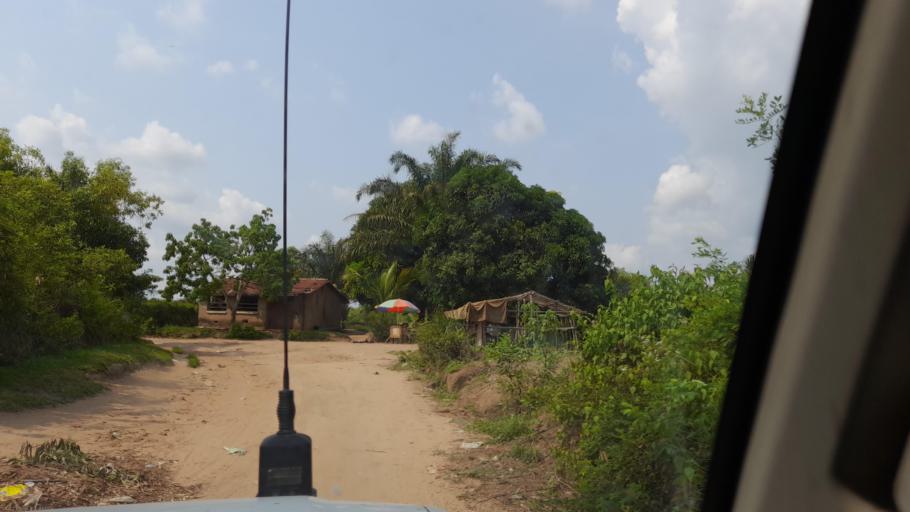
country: CD
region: Kasai-Occidental
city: Kananga
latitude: -5.9048
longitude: 22.4754
